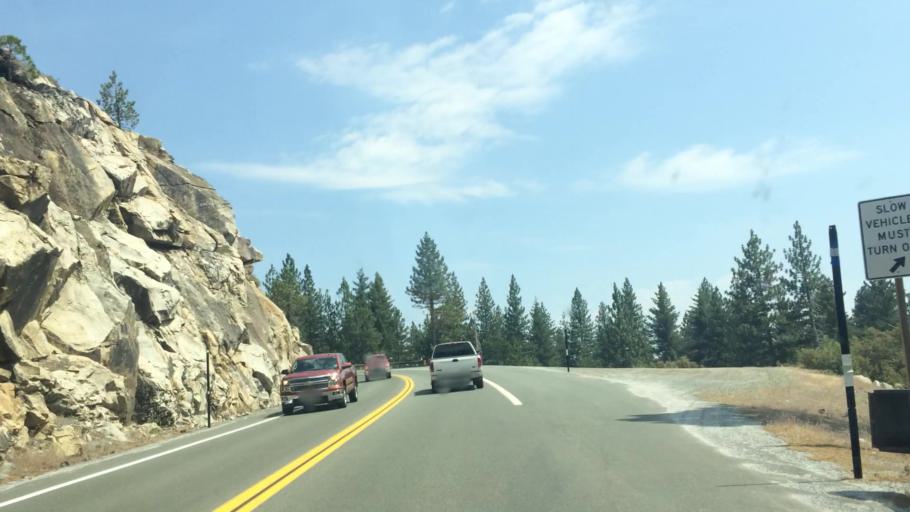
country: US
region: California
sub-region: Amador County
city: Pioneer
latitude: 38.5425
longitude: -120.3475
